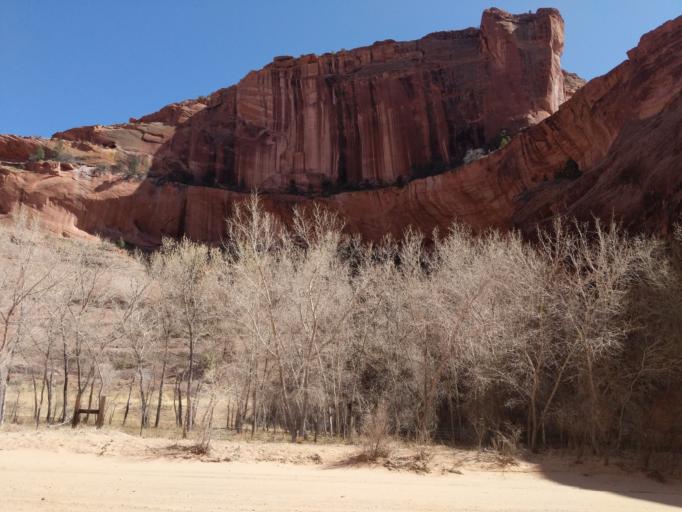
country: US
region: Arizona
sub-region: Apache County
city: Chinle
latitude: 36.1520
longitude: -109.4738
